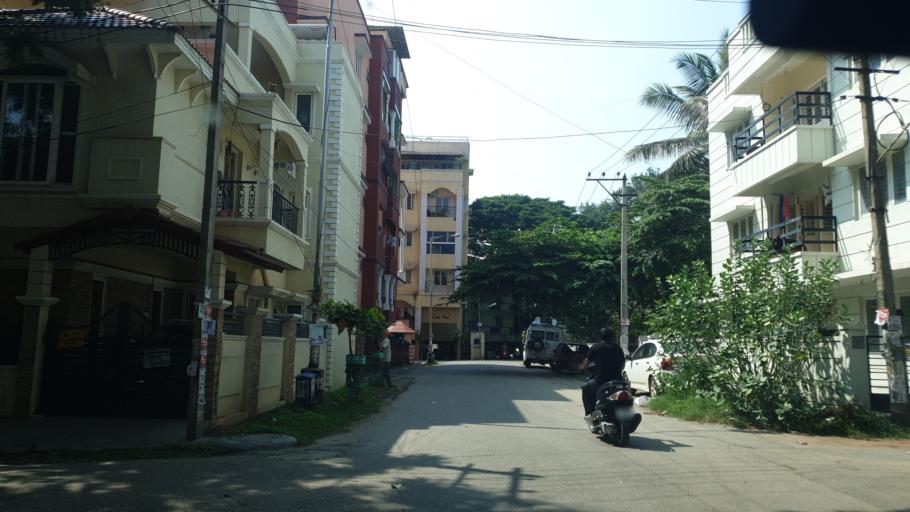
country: IN
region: Karnataka
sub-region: Bangalore Urban
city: Bangalore
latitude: 12.9834
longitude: 77.6654
